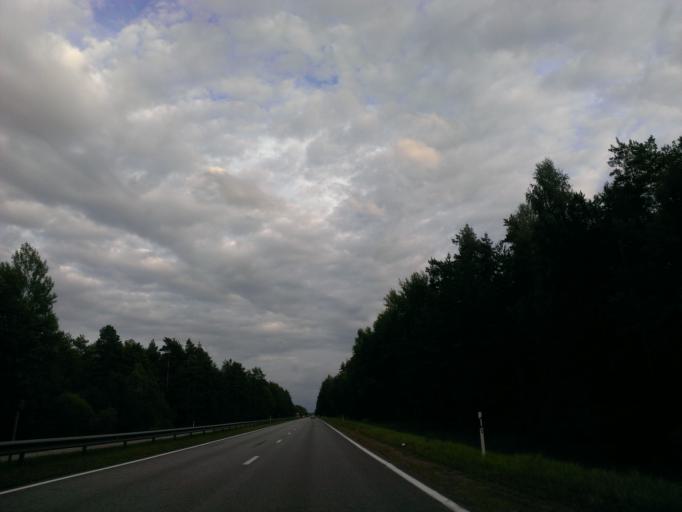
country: LV
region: Ikskile
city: Ikskile
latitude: 56.8339
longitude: 24.5050
